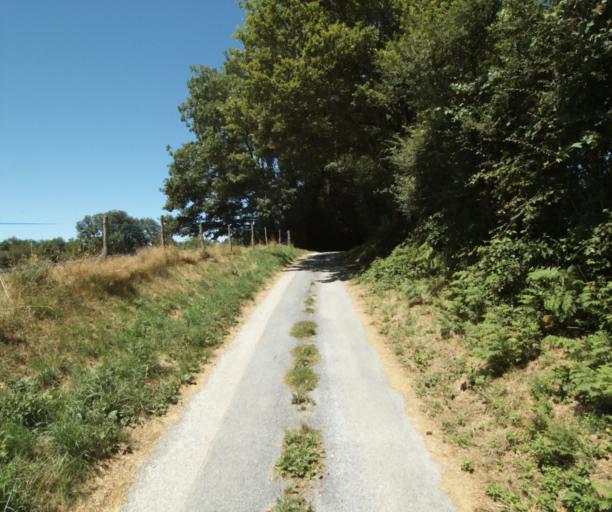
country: FR
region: Midi-Pyrenees
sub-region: Departement du Tarn
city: Dourgne
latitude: 43.4294
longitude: 2.1740
